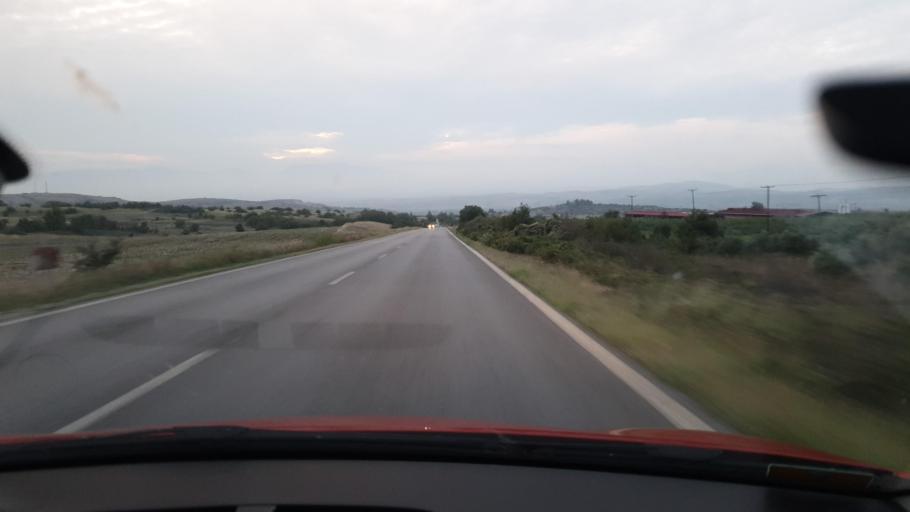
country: GR
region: Central Macedonia
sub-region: Nomos Kilkis
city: Polykastro
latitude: 41.0087
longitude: 22.6846
